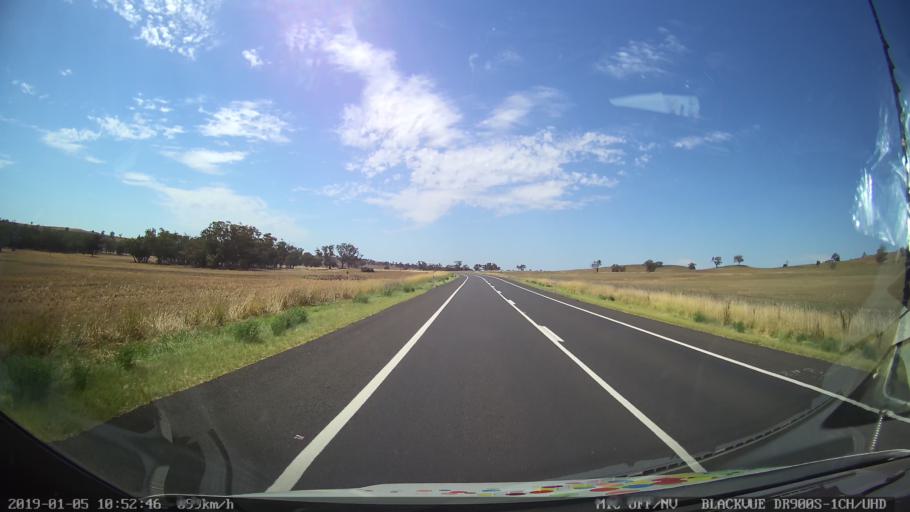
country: AU
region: New South Wales
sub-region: Warrumbungle Shire
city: Coonabarabran
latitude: -31.4359
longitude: 149.1057
